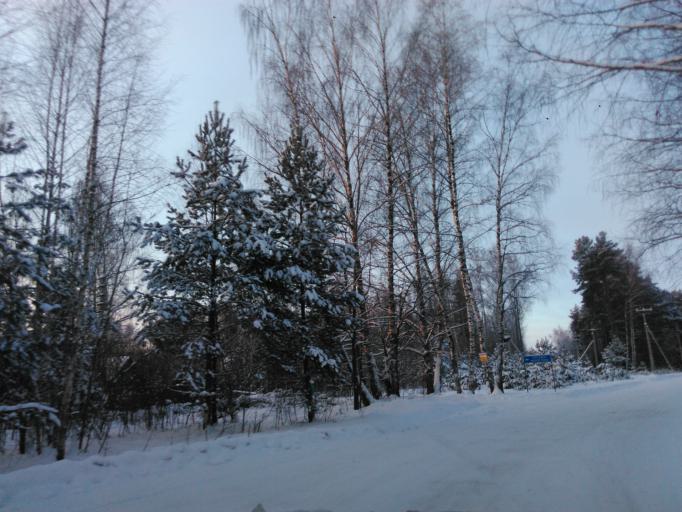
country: RU
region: Tverskaya
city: Konakovo
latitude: 56.6507
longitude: 36.6548
